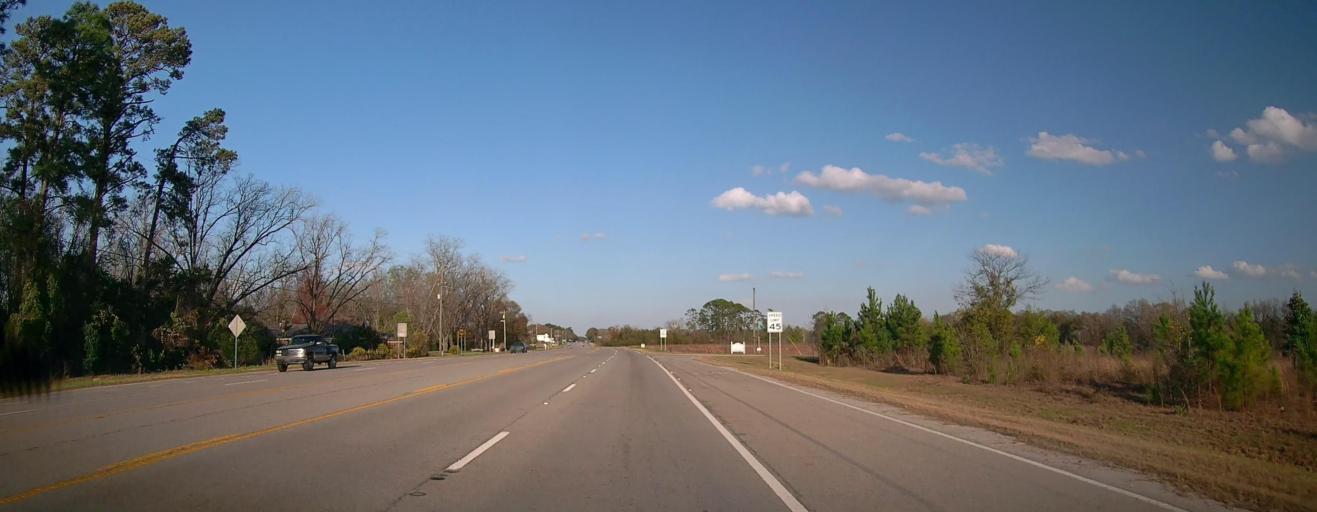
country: US
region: Georgia
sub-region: Evans County
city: Claxton
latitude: 32.1531
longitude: -81.9537
